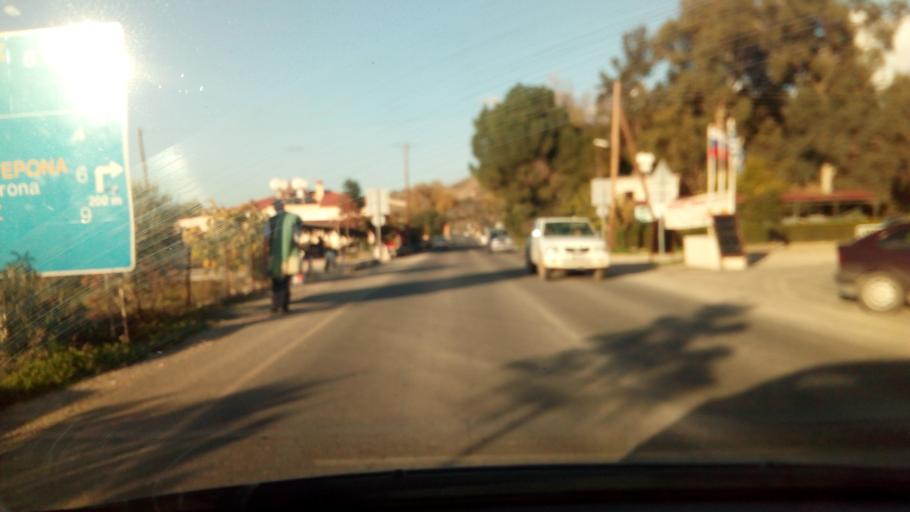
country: CY
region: Pafos
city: Polis
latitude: 34.9811
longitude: 32.4514
